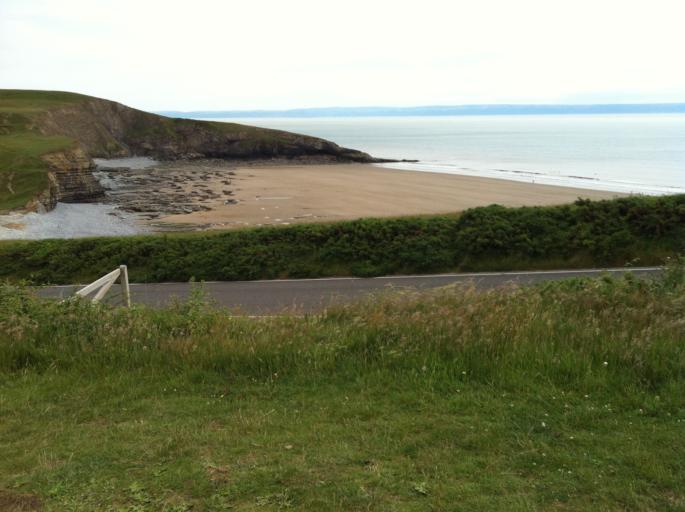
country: GB
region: Wales
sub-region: Bridgend county borough
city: Merthyr Mawr
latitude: 51.4475
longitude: -3.6071
